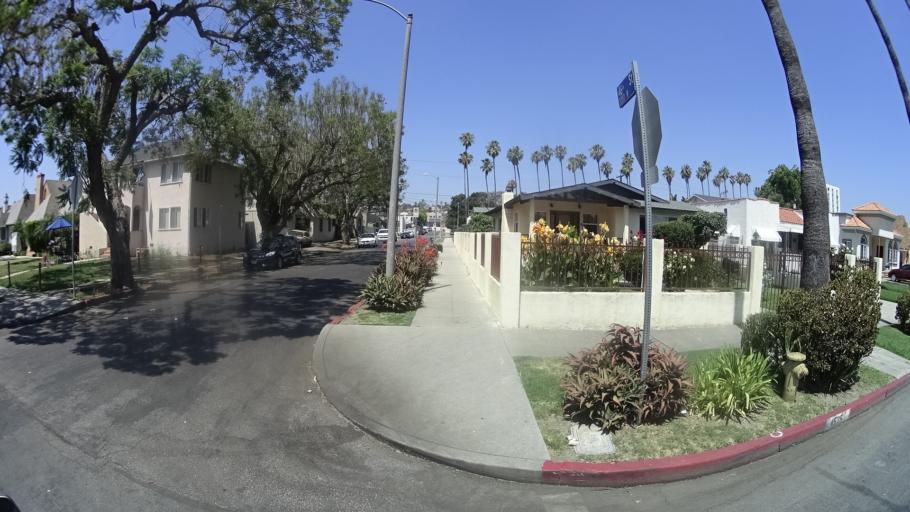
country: US
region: California
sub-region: Los Angeles County
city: View Park-Windsor Hills
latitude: 34.0019
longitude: -118.3282
